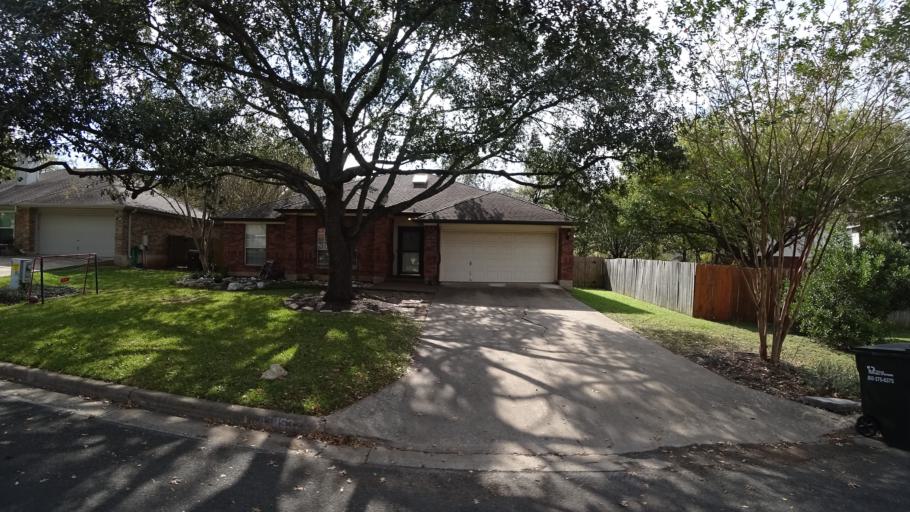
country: US
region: Texas
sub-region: Travis County
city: Shady Hollow
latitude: 30.1594
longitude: -97.8533
